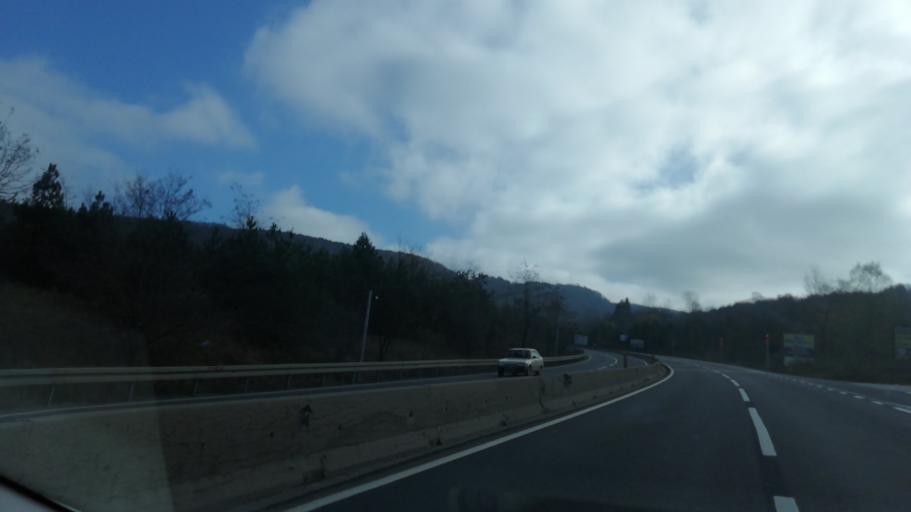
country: TR
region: Duzce
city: Kaynasli
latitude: 40.7486
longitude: 31.3762
